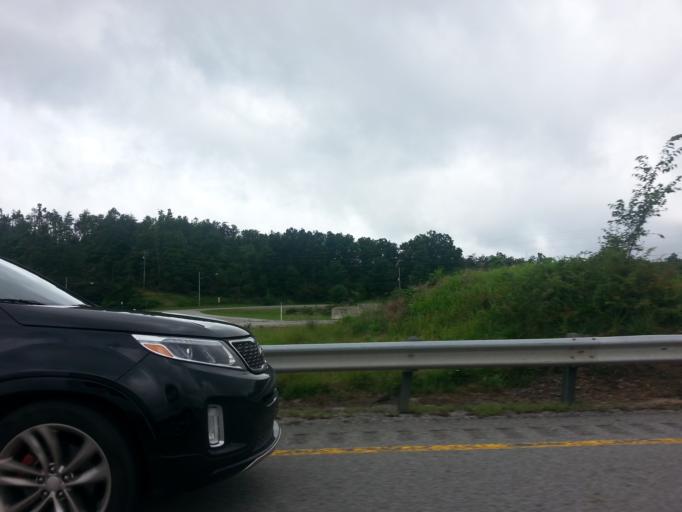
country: US
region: Tennessee
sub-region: Putnam County
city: Monterey
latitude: 36.1385
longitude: -85.2664
